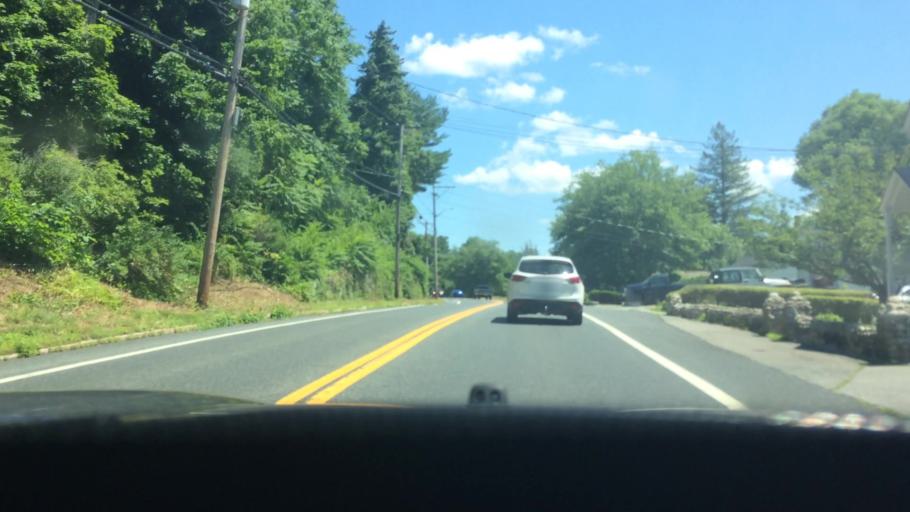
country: US
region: Massachusetts
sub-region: Worcester County
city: Blackstone
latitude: 41.9984
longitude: -71.5481
